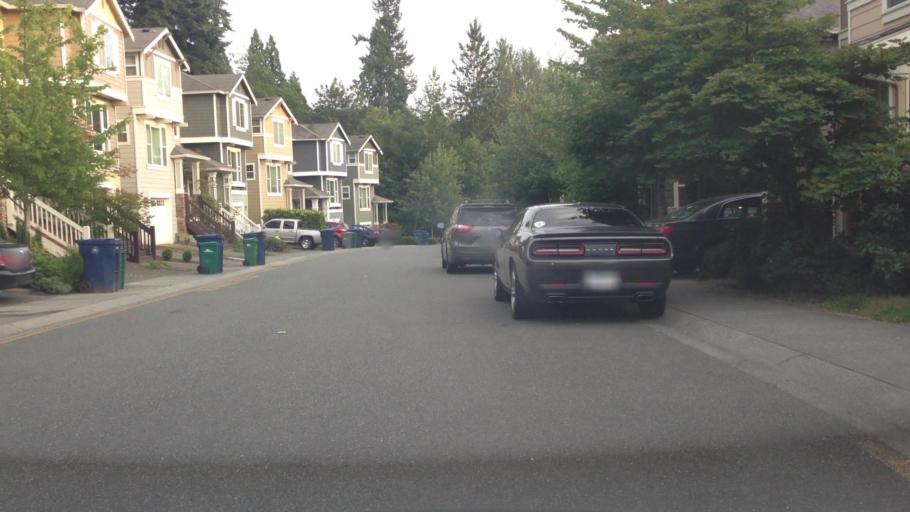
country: US
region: Washington
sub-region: King County
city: Woodinville
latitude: 47.7630
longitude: -122.1478
